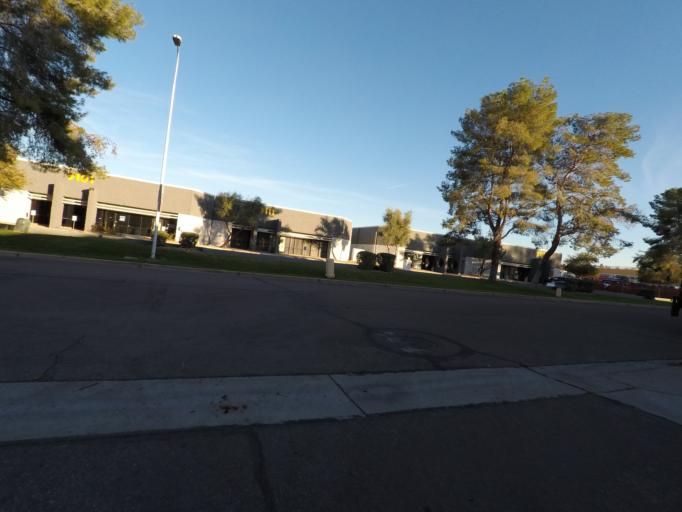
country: US
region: Arizona
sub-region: Maricopa County
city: Guadalupe
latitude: 33.3956
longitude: -111.9741
